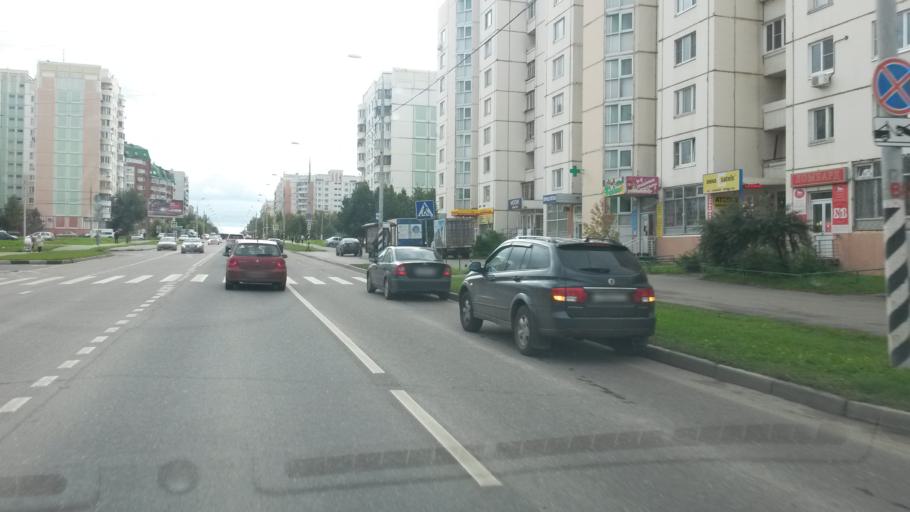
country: RU
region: Moskovskaya
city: Kommunarka
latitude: 55.5359
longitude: 37.5152
